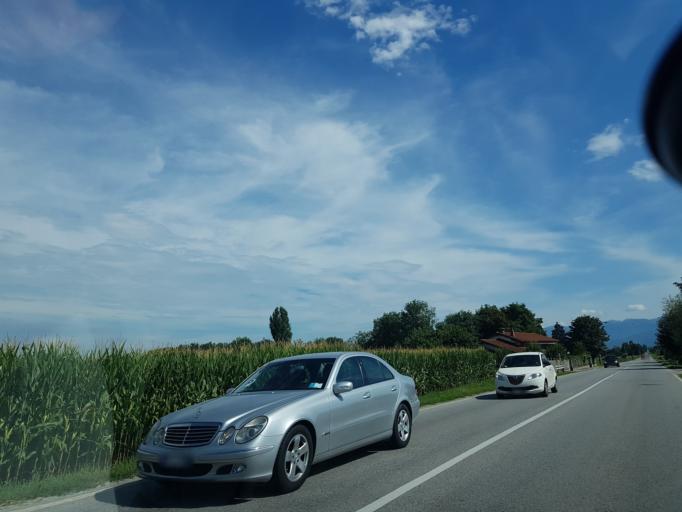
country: IT
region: Piedmont
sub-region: Provincia di Cuneo
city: Roata Rossi
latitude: 44.4654
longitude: 7.5153
